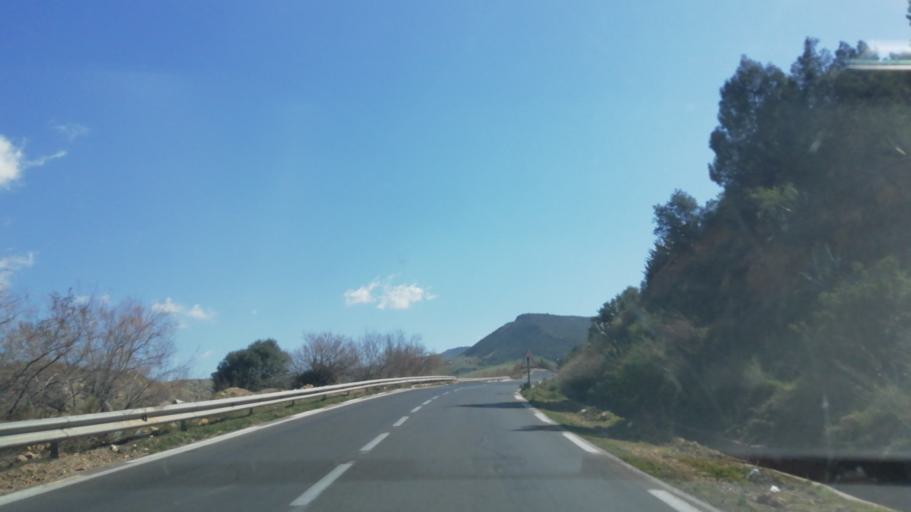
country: DZ
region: Mascara
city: Mascara
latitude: 35.5006
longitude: 0.1312
